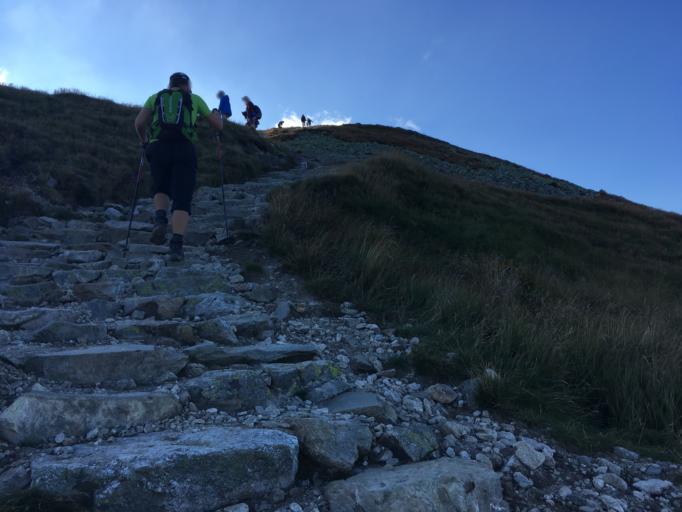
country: PL
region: Lesser Poland Voivodeship
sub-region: Powiat tatrzanski
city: Zakopane
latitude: 49.2360
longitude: 19.9332
